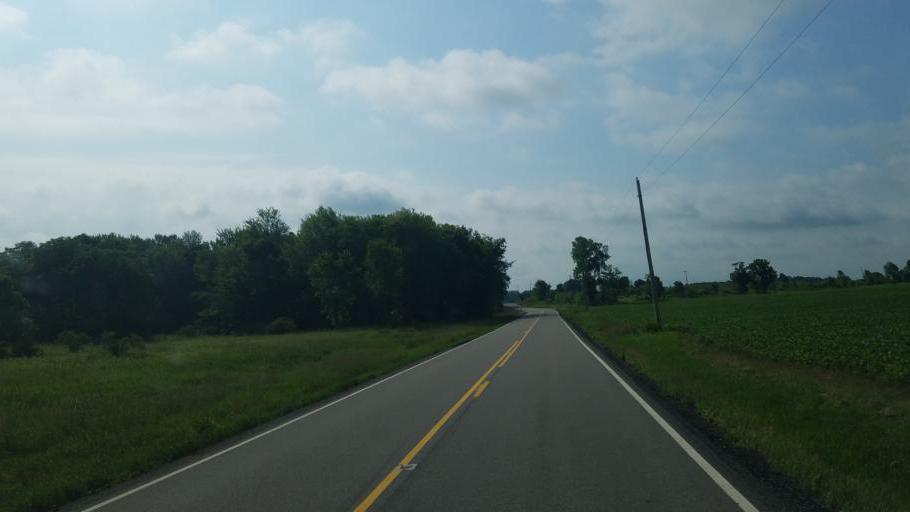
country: US
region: Ohio
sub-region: Knox County
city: Centerburg
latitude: 40.3084
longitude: -82.6512
